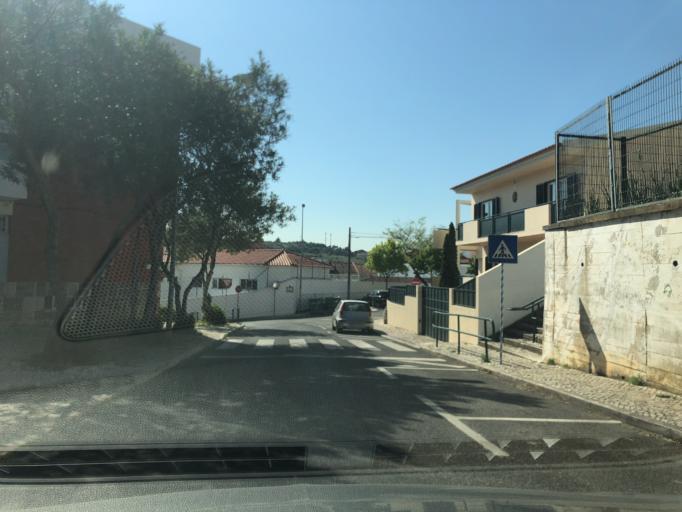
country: PT
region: Lisbon
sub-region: Oeiras
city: Terrugem
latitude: 38.7070
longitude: -9.2761
